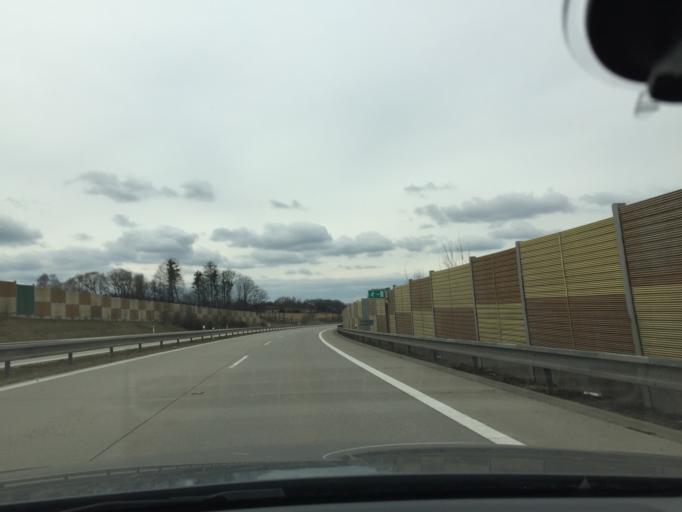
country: CZ
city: Chotebuz
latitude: 49.7156
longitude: 18.5581
